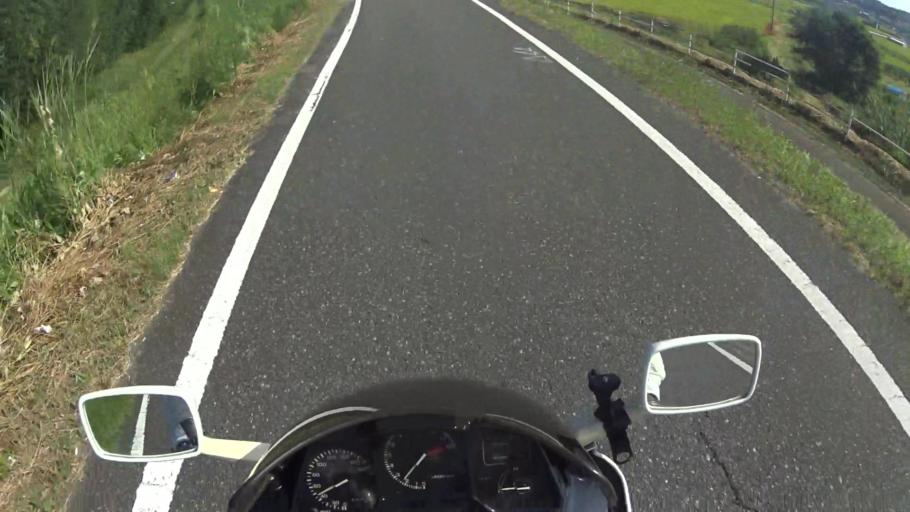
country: JP
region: Kyoto
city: Tanabe
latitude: 34.8322
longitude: 135.7626
